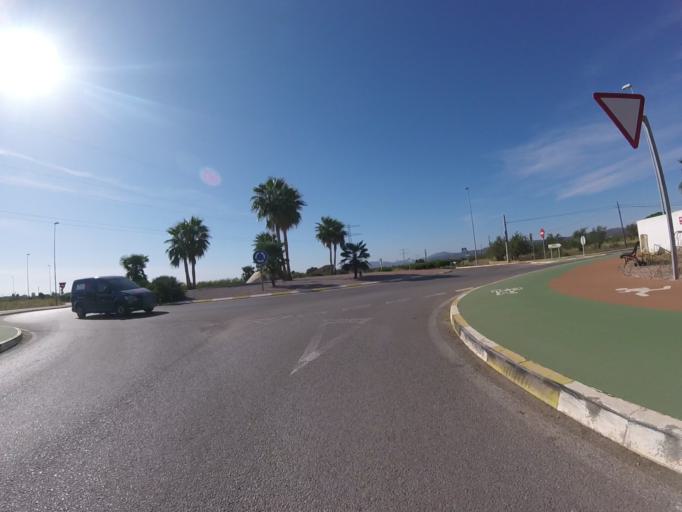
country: ES
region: Valencia
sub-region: Provincia de Castello
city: Torreblanca
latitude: 40.2093
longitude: 0.2084
